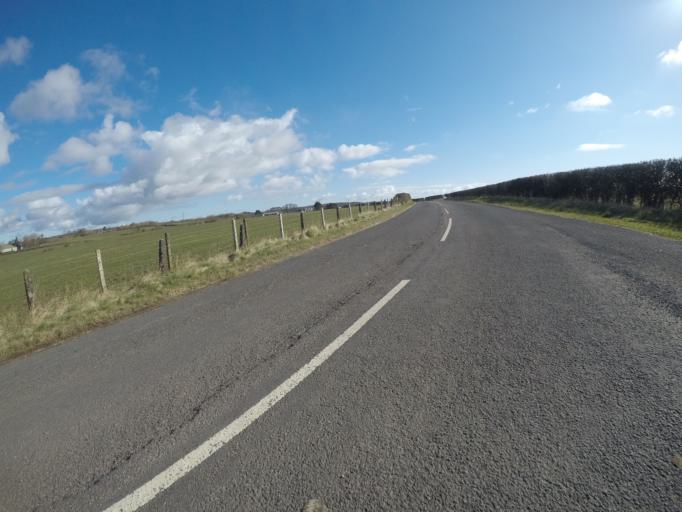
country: GB
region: Scotland
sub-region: North Ayrshire
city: Irvine
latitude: 55.6521
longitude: -4.6568
